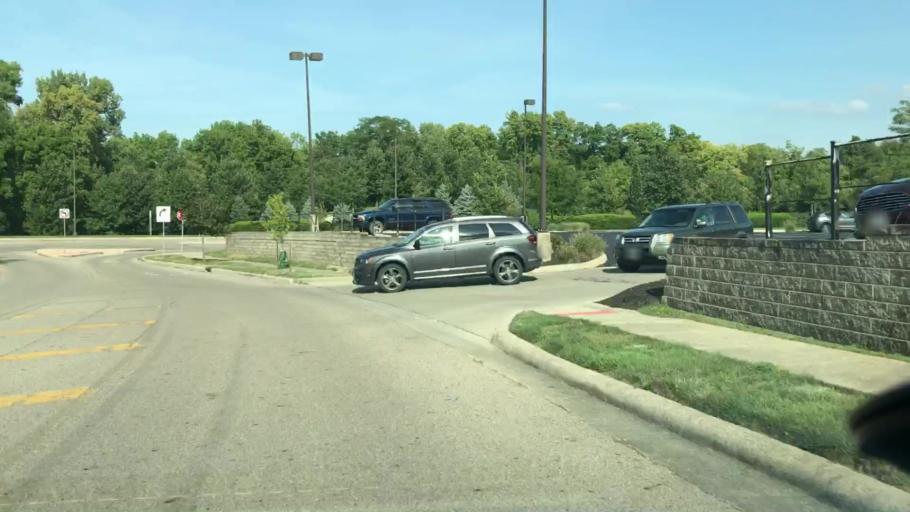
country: US
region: Ohio
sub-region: Franklin County
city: Hilliard
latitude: 40.0349
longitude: -83.1187
